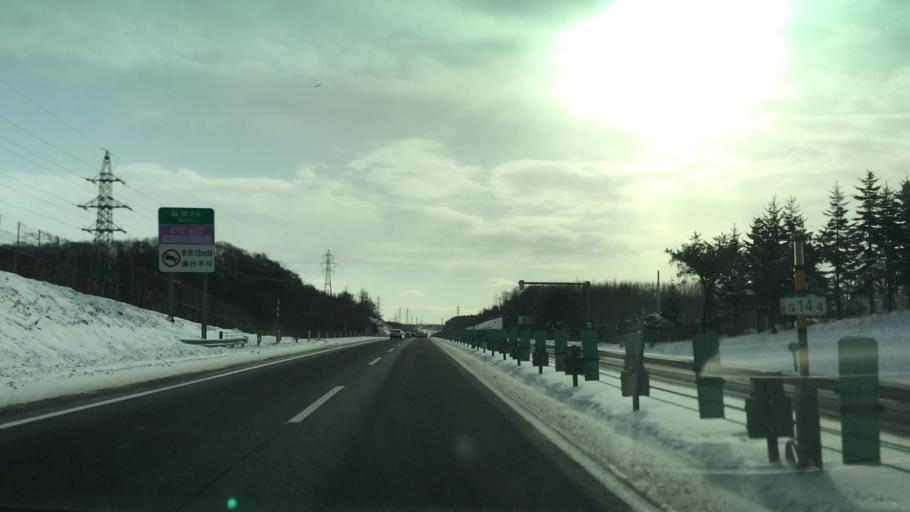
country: JP
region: Hokkaido
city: Kitahiroshima
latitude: 42.9641
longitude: 141.4962
